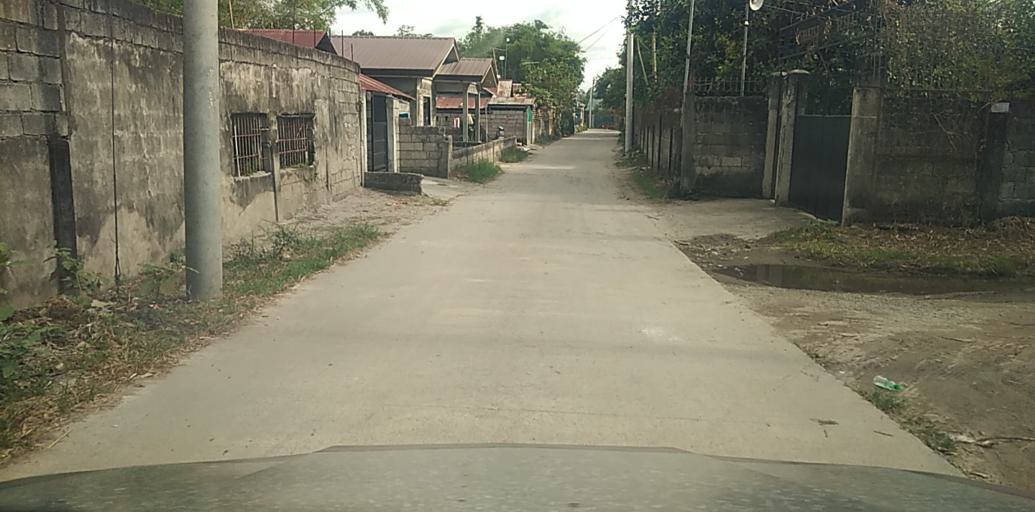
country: PH
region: Central Luzon
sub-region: Province of Pampanga
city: Panlinlang
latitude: 15.1851
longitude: 120.6952
